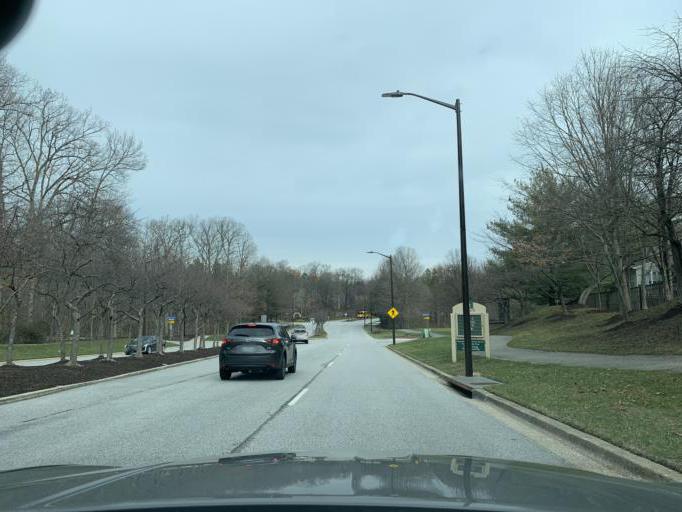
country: US
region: Maryland
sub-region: Anne Arundel County
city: Maryland City
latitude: 39.1005
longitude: -76.8098
